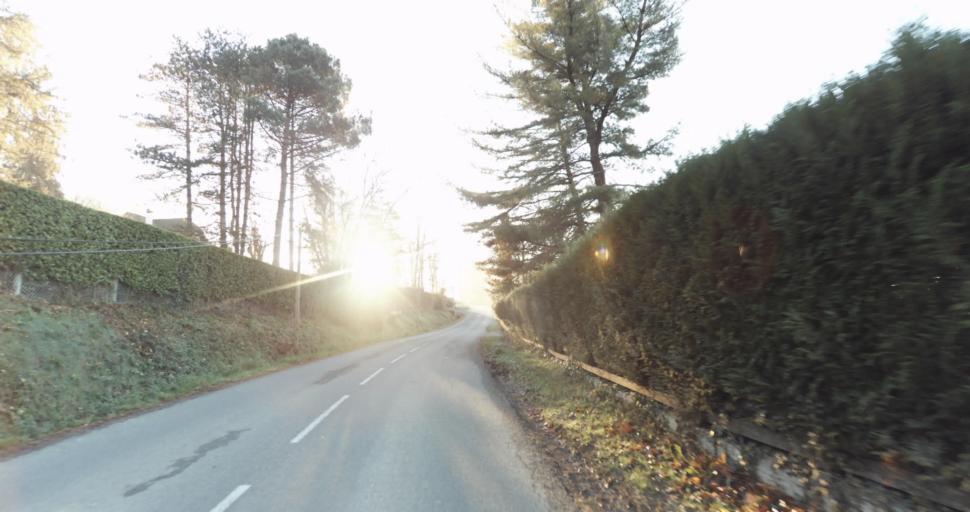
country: FR
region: Aquitaine
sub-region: Departement des Pyrenees-Atlantiques
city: Morlaas
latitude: 43.3299
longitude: -0.2705
